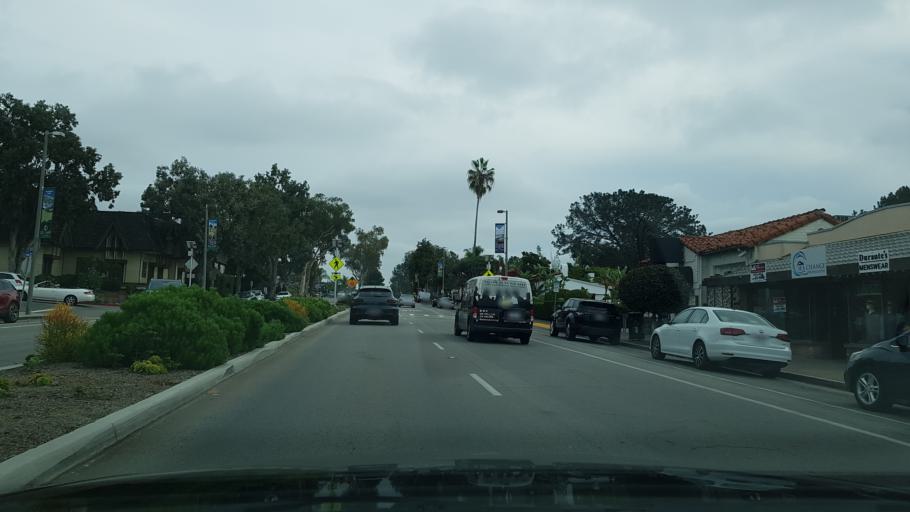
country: US
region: California
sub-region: San Diego County
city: Del Mar
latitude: 32.9590
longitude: -117.2651
